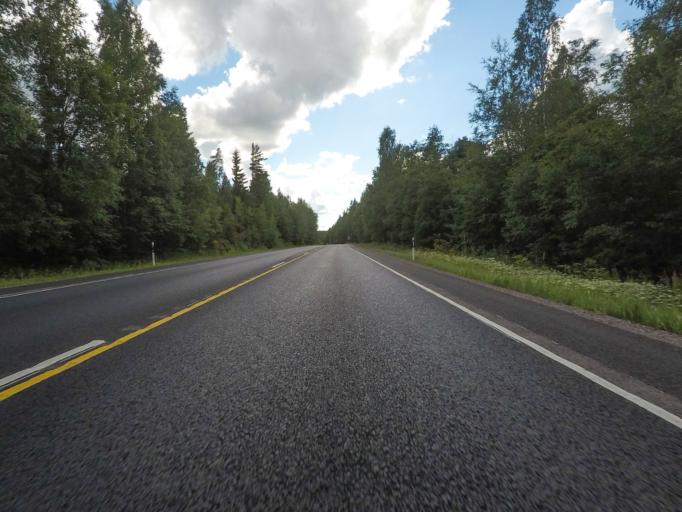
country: FI
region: Uusimaa
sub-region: Helsinki
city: Nurmijaervi
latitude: 60.4930
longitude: 24.5987
